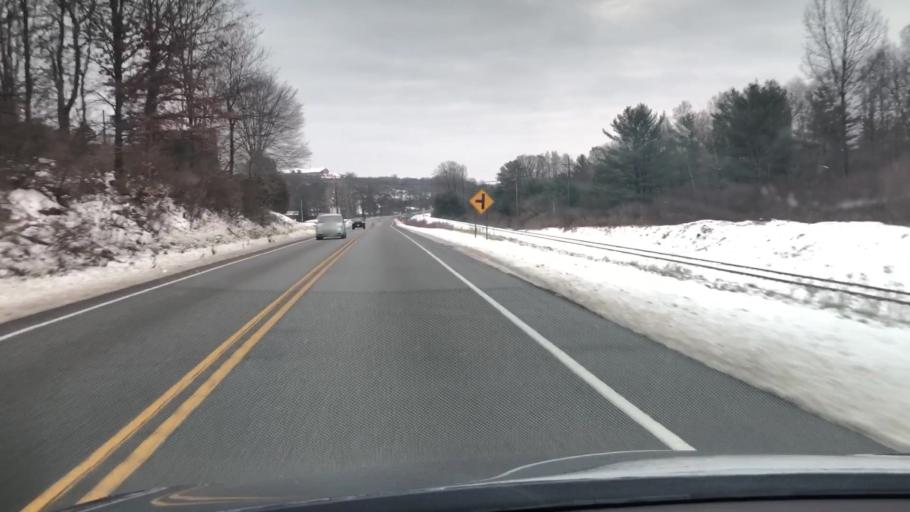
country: US
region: Pennsylvania
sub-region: Clearfield County
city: Treasure Lake
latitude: 41.1343
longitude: -78.7004
